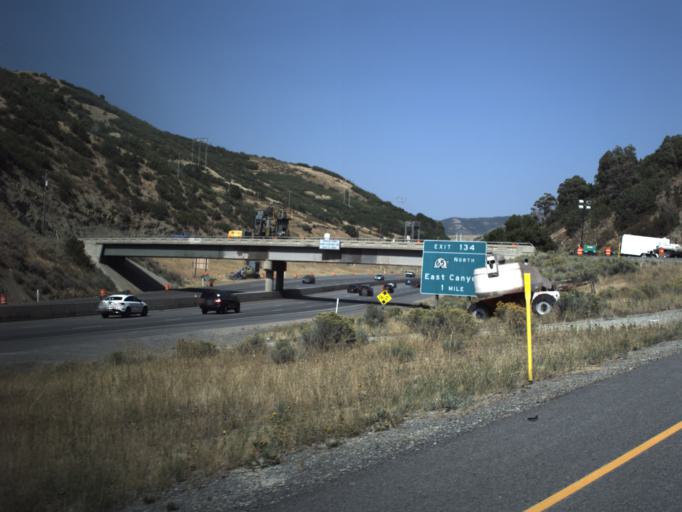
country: US
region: Utah
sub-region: Salt Lake County
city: Mount Olympus
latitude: 40.7428
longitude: -111.7320
